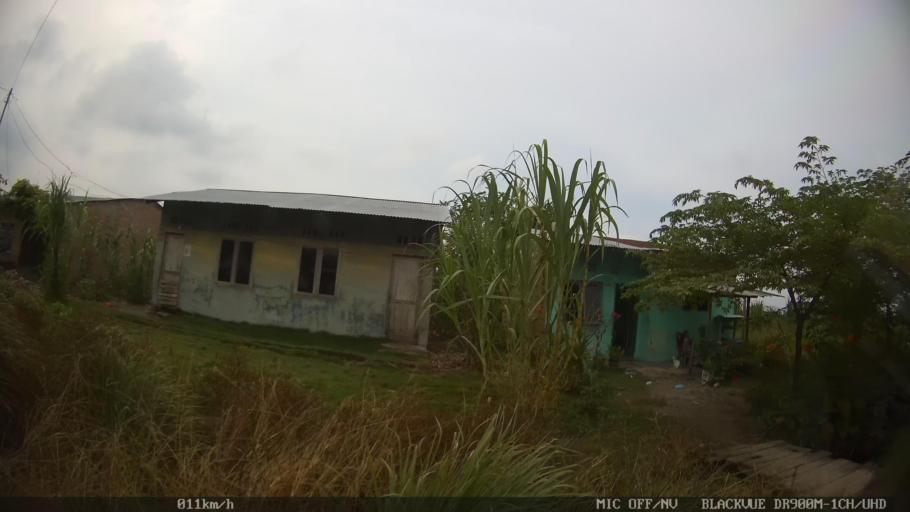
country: ID
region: North Sumatra
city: Medan
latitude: 3.5734
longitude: 98.7404
